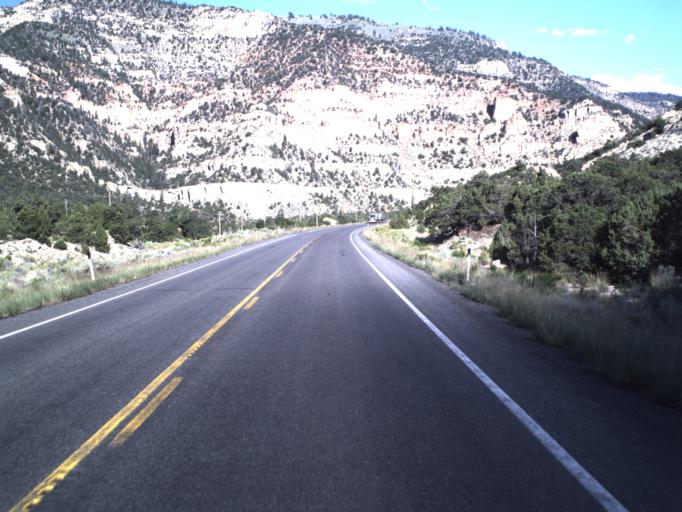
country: US
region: Utah
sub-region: Emery County
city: Huntington
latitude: 39.3930
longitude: -111.0975
